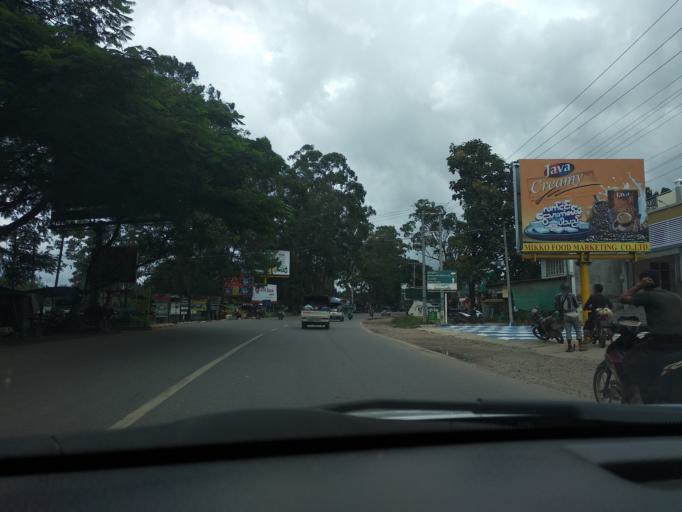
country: MM
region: Mandalay
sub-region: Pyin Oo Lwin District
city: Pyin Oo Lwin
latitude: 21.9770
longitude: 96.4075
